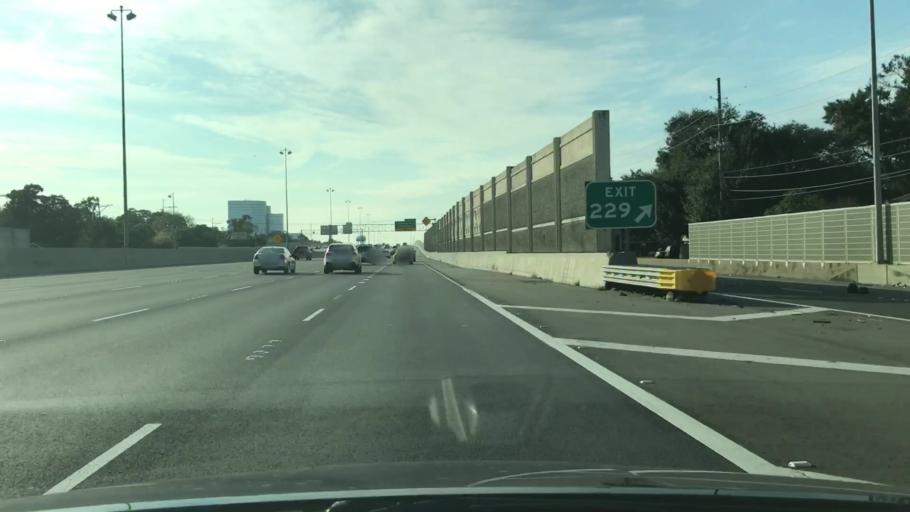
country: US
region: Louisiana
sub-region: Jefferson Parish
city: Metairie
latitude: 29.9972
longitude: -90.1385
